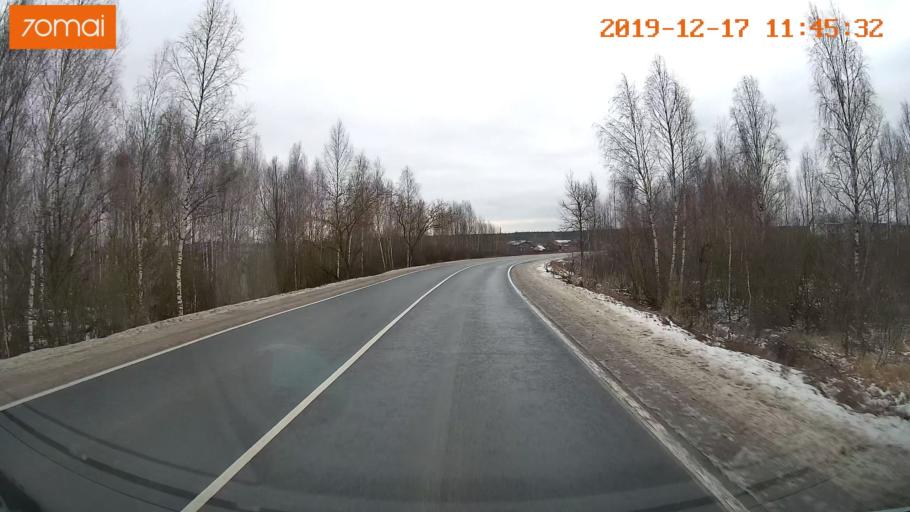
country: RU
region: Vladimir
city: Velikodvorskiy
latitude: 55.2501
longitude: 40.6743
